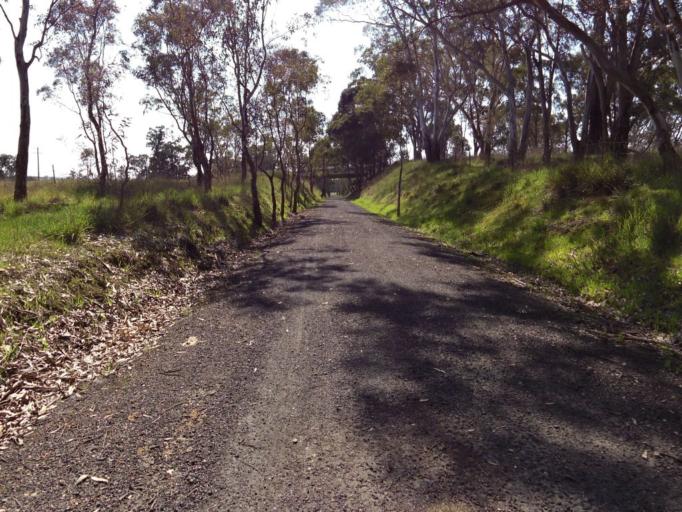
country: AU
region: Victoria
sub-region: Murrindindi
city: Alexandra
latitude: -37.1173
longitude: 145.6051
